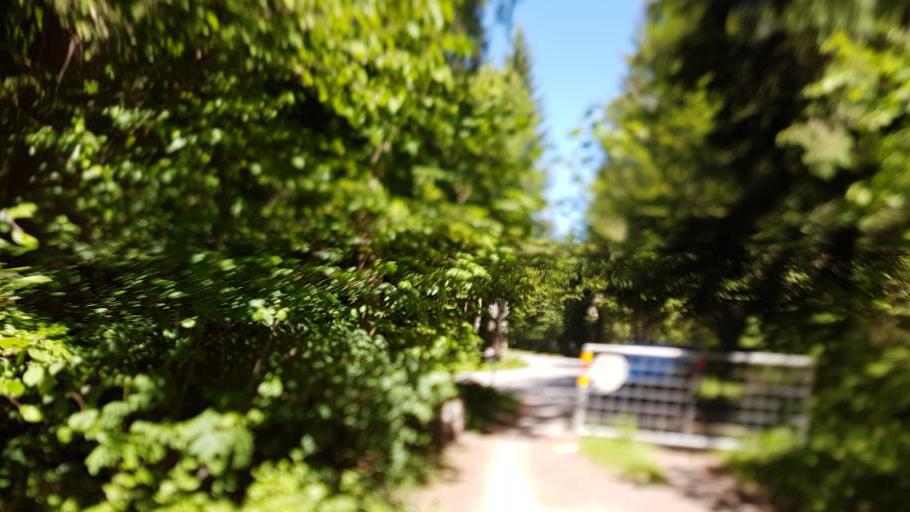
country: CH
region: Bern
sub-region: Thun District
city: Thun
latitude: 46.7225
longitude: 7.6051
